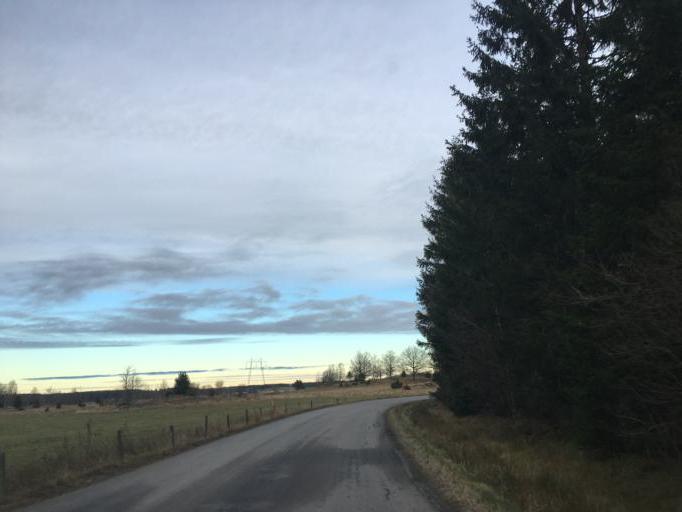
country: SE
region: OEstergoetland
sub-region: Norrkopings Kommun
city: Kimstad
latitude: 58.4319
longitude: 16.0708
